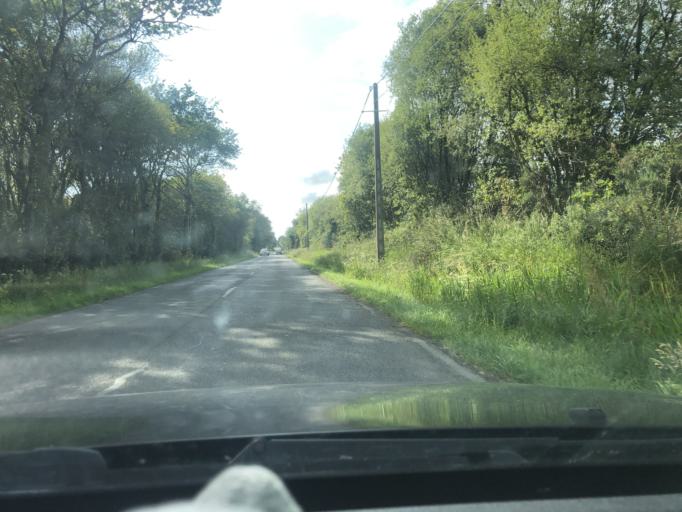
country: FR
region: Brittany
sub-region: Departement du Morbihan
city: Sainte-Helene
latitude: 47.6899
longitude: -3.2305
